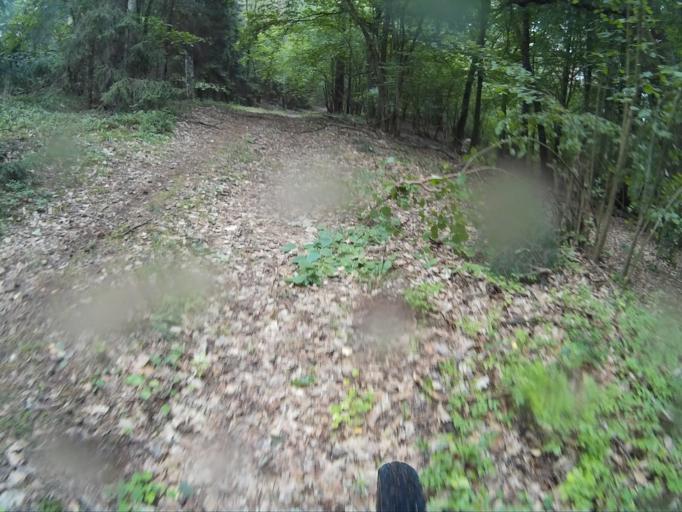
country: PL
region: Kujawsko-Pomorskie
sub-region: Powiat tucholski
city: Tuchola
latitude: 53.5811
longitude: 17.9081
